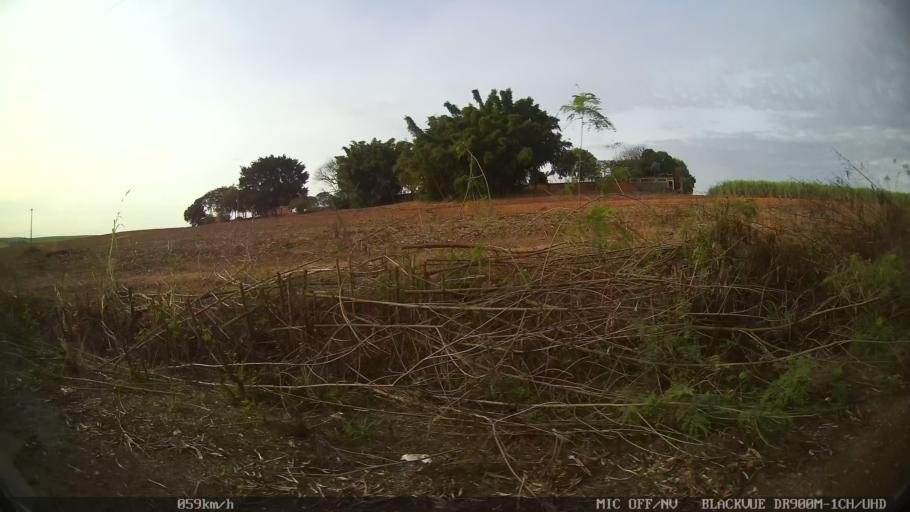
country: BR
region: Sao Paulo
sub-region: Piracicaba
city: Piracicaba
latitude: -22.7051
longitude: -47.5849
